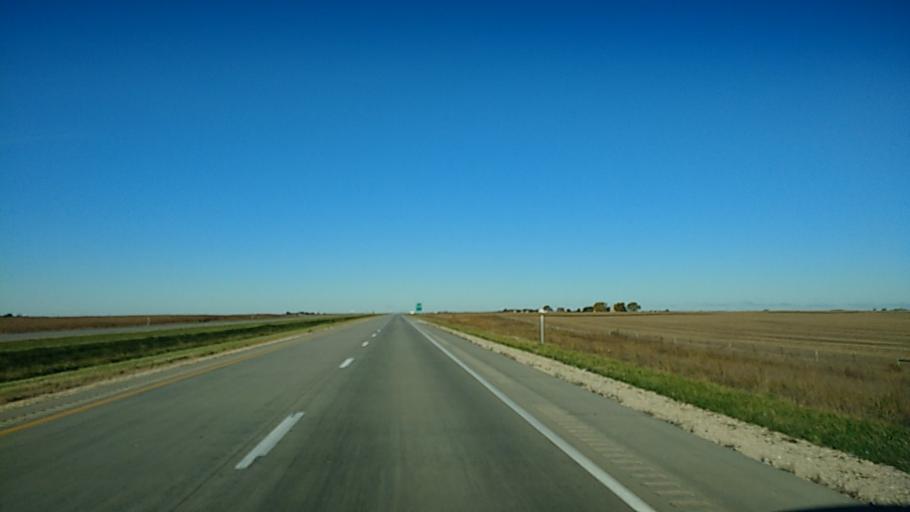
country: US
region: Iowa
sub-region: Sac County
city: Sac City
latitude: 42.4542
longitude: -94.9191
